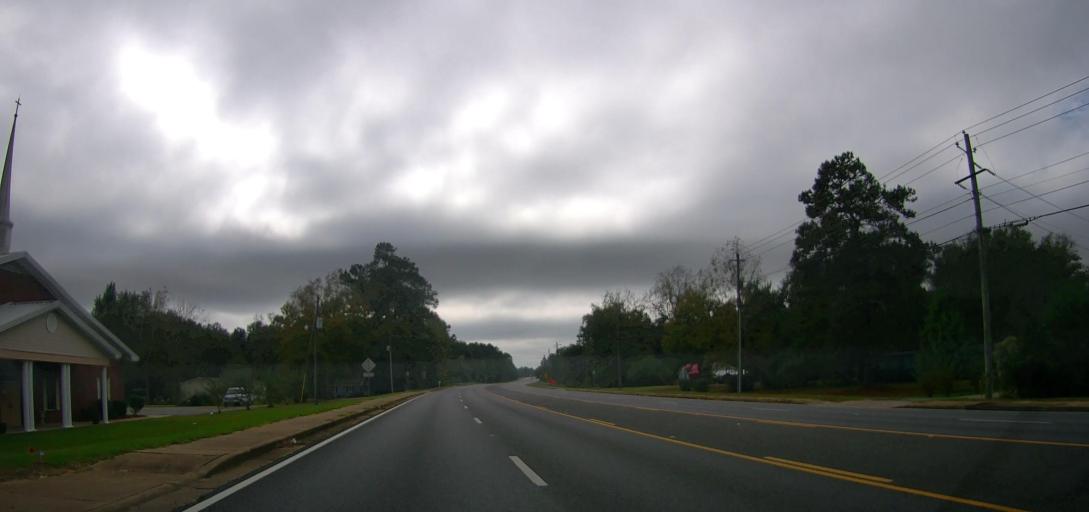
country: US
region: Georgia
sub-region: Colquitt County
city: Moultrie
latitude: 31.0041
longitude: -83.8687
